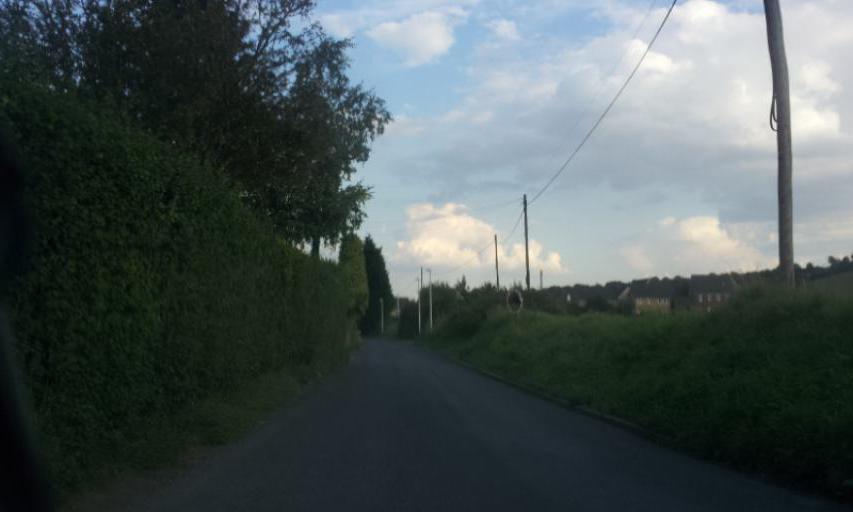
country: GB
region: England
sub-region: Medway
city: Cuxton
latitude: 51.3784
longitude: 0.4422
